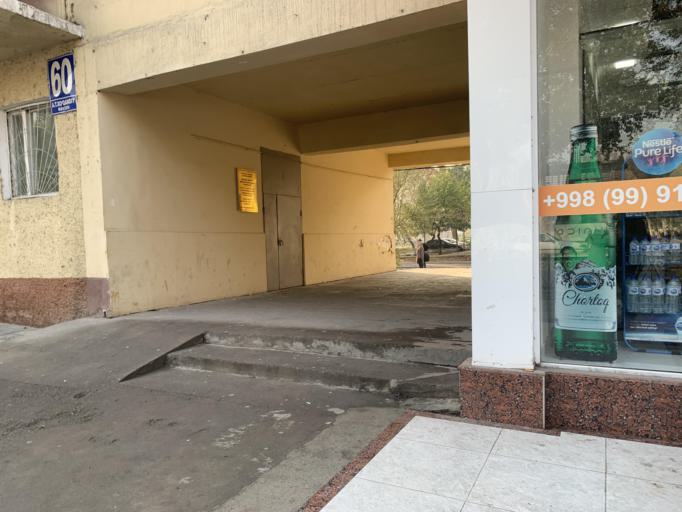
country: UZ
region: Fergana
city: Qo`qon
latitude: 40.5481
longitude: 70.9246
